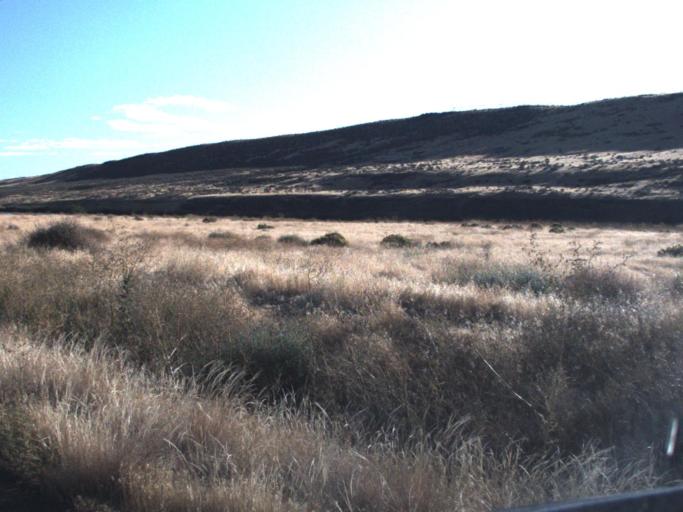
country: US
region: Washington
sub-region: Benton County
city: Benton City
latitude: 46.3418
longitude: -119.4755
